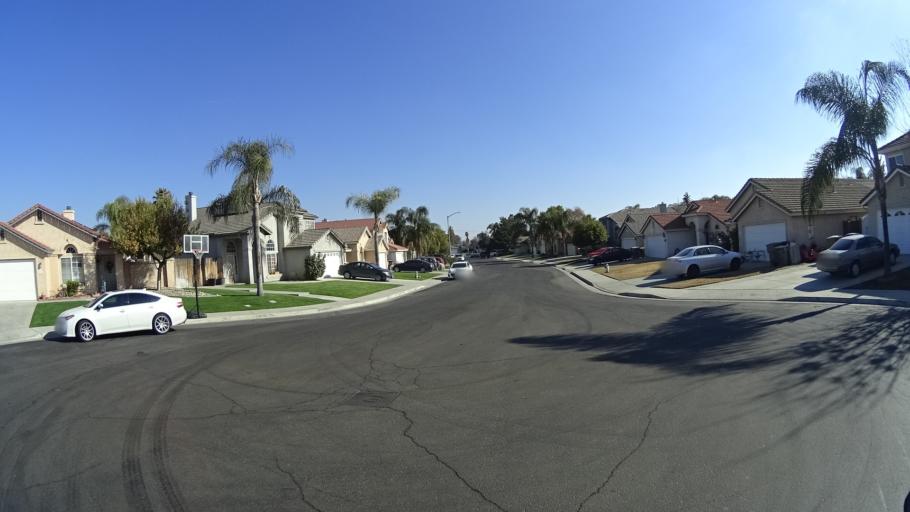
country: US
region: California
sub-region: Kern County
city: Greenfield
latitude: 35.2997
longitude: -119.0593
